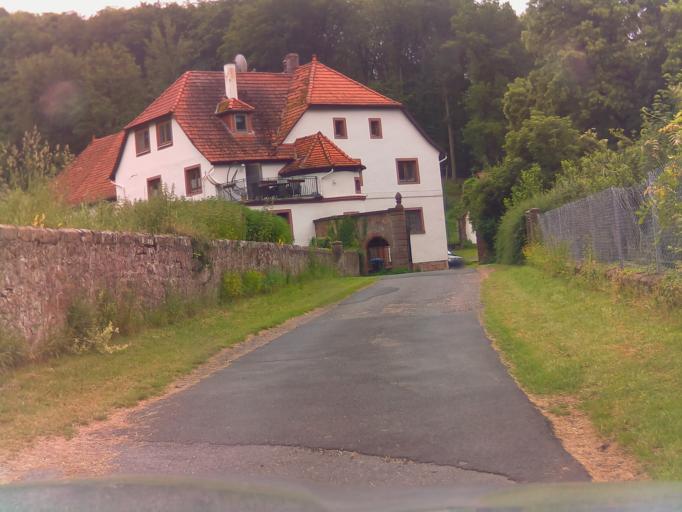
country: DE
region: Bavaria
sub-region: Regierungsbezirk Unterfranken
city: Eschau
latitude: 49.8387
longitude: 9.2930
